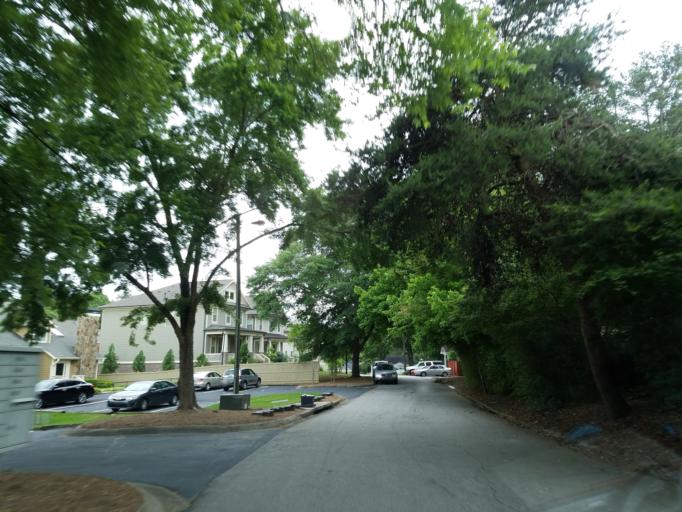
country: US
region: Georgia
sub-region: Cobb County
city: Smyrna
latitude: 33.8880
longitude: -84.5083
